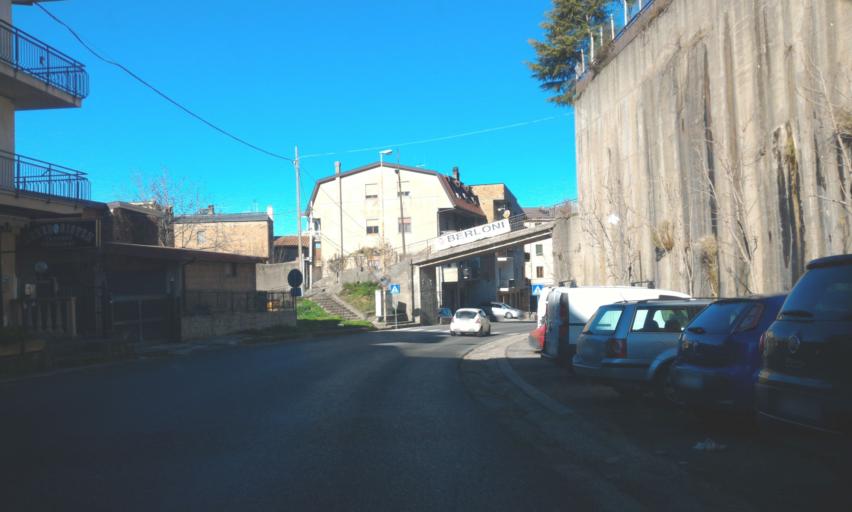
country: IT
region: Calabria
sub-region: Provincia di Cosenza
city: Spezzano della Sila
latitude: 39.3005
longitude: 16.3411
